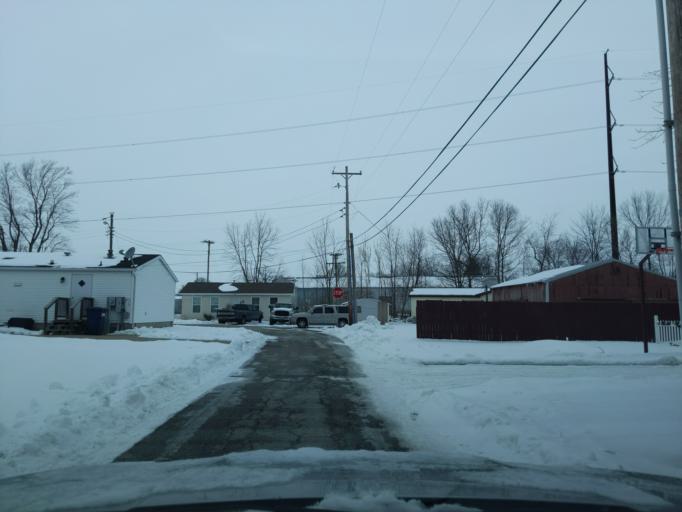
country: US
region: Indiana
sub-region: Benton County
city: Otterbein
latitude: 40.4872
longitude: -87.0938
